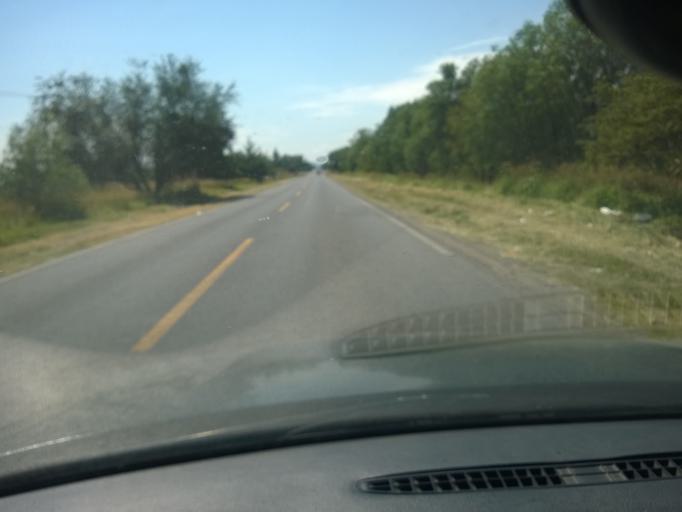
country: MX
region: Guanajuato
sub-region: Leon
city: Plan Guanajuato (La Sandia)
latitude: 20.9716
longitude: -101.7025
